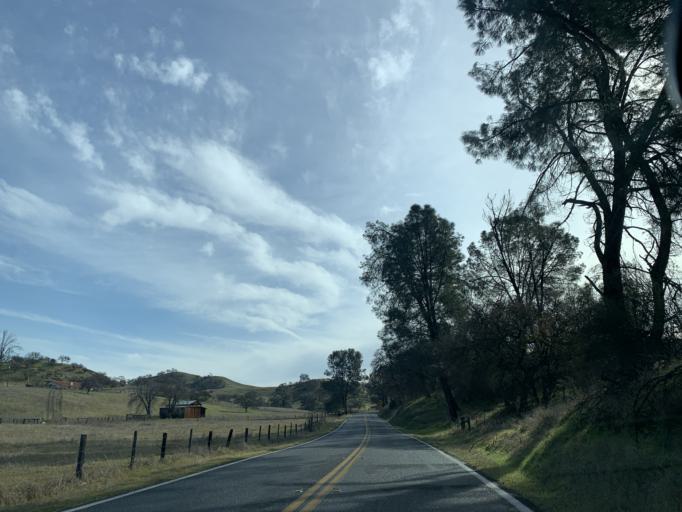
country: US
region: California
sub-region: Monterey County
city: Greenfield
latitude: 36.5085
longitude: -121.1122
